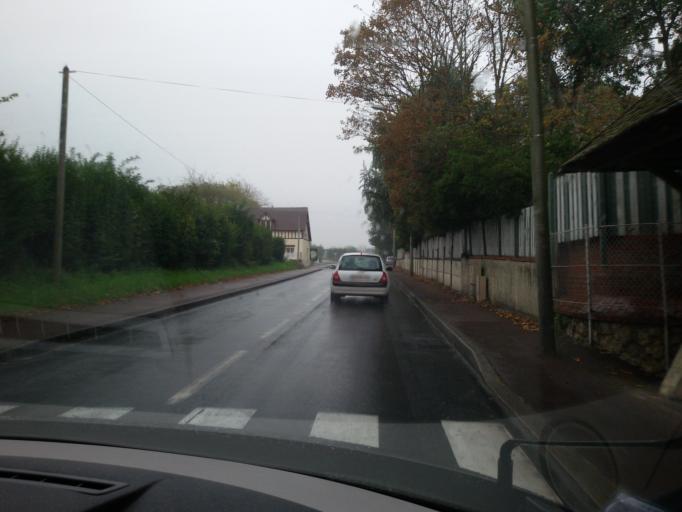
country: FR
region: Lower Normandy
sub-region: Departement du Calvados
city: Blonville-sur-Mer
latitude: 49.3446
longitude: 0.0408
